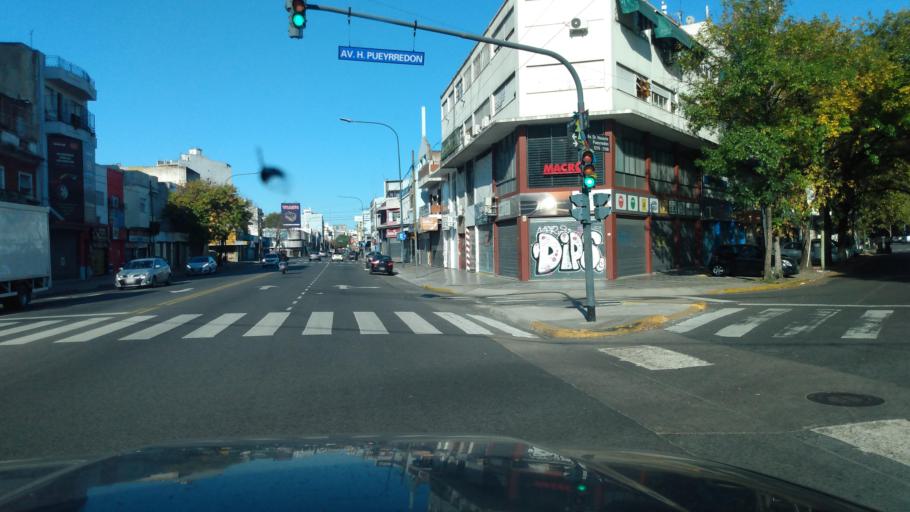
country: AR
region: Buenos Aires F.D.
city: Colegiales
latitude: -34.5987
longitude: -58.4530
